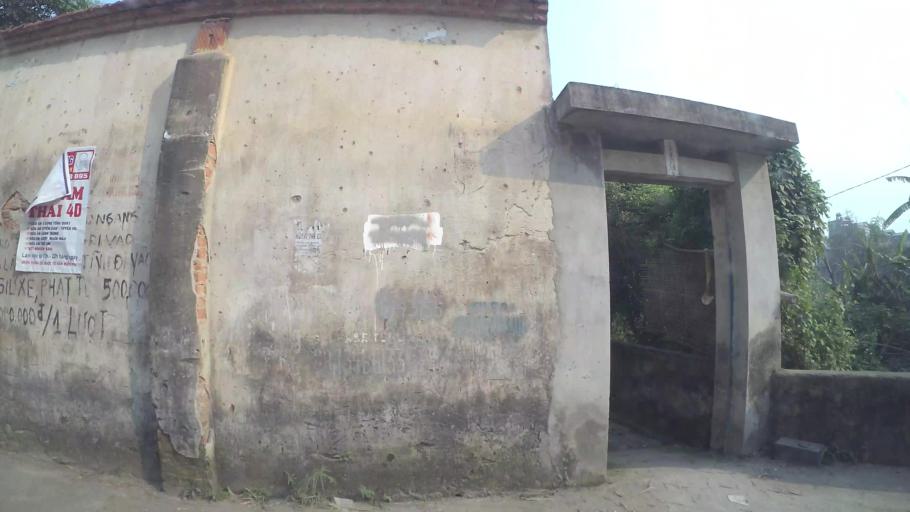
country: VN
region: Ha Noi
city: Ha Dong
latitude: 20.9311
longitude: 105.7974
